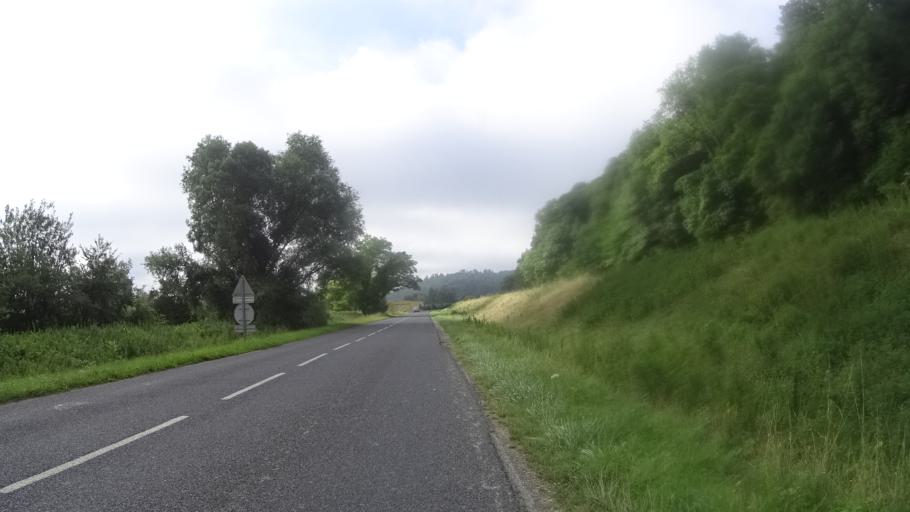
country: FR
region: Lorraine
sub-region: Departement de la Meuse
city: Fains-Veel
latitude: 48.8012
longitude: 5.1105
